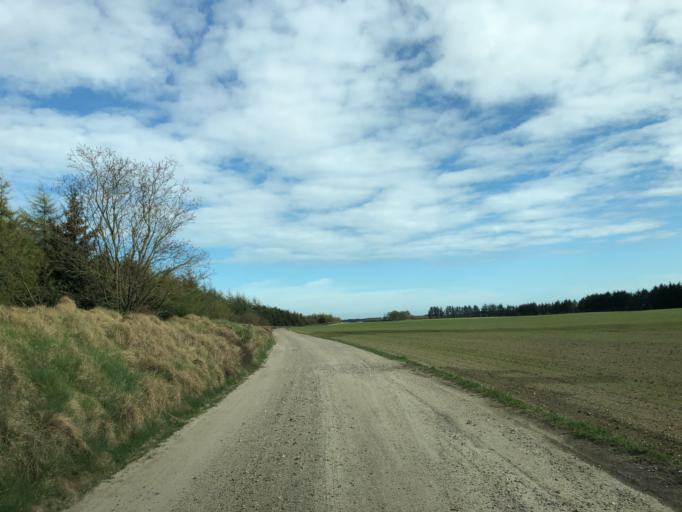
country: DK
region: Central Jutland
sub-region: Holstebro Kommune
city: Ulfborg
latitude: 56.2479
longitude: 8.3355
